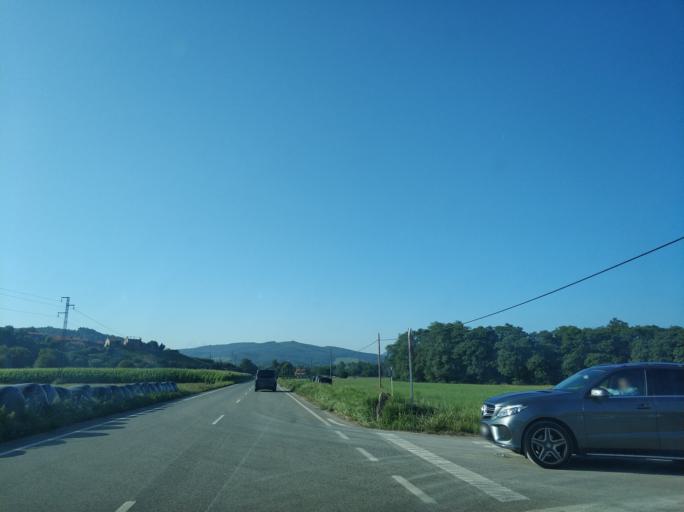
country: ES
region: Cantabria
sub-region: Provincia de Cantabria
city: Polanco
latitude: 43.3775
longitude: -3.9642
